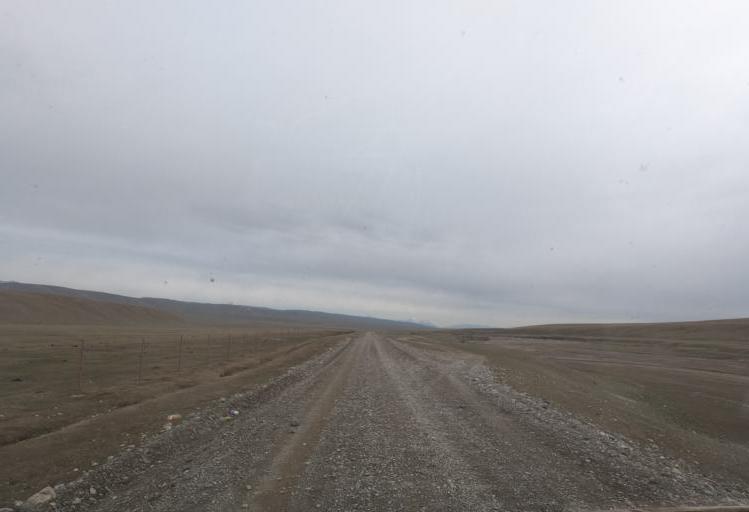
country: KG
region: Naryn
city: Baetov
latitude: 40.9111
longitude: 75.2694
